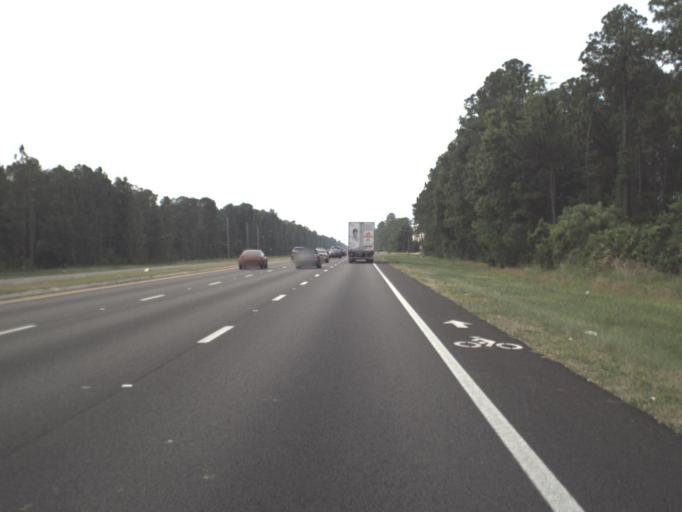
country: US
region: Florida
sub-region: Saint Johns County
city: Fruit Cove
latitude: 30.0956
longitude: -81.7061
